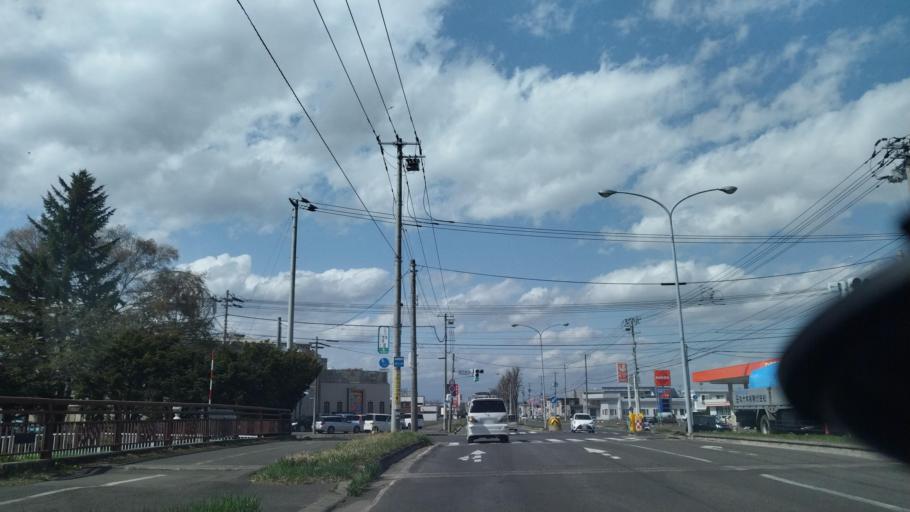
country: JP
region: Hokkaido
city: Obihiro
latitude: 42.9073
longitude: 143.1458
